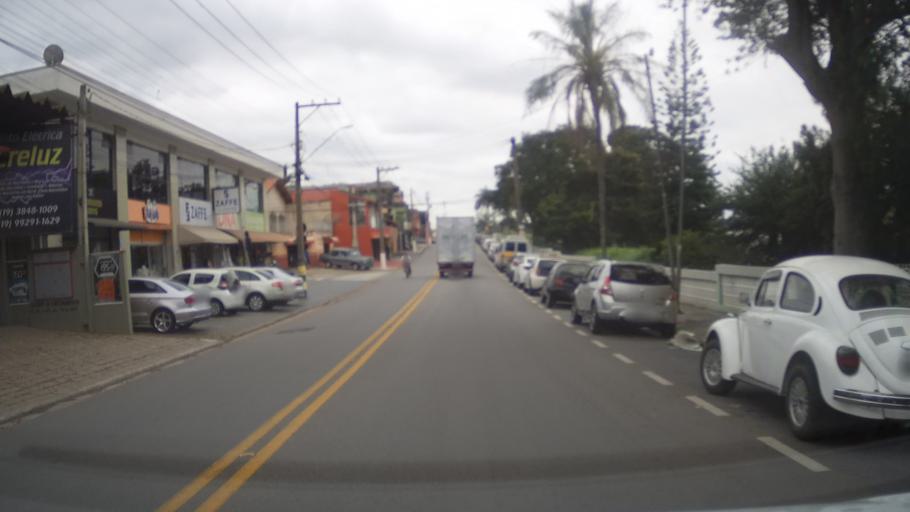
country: BR
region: Sao Paulo
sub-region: Louveira
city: Louveira
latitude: -23.0882
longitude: -46.9749
